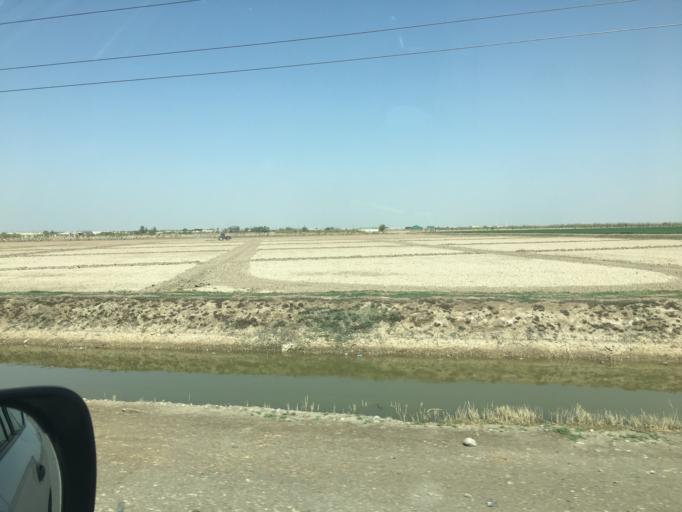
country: TM
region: Lebap
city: Turkmenabat
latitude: 38.9822
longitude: 63.6401
